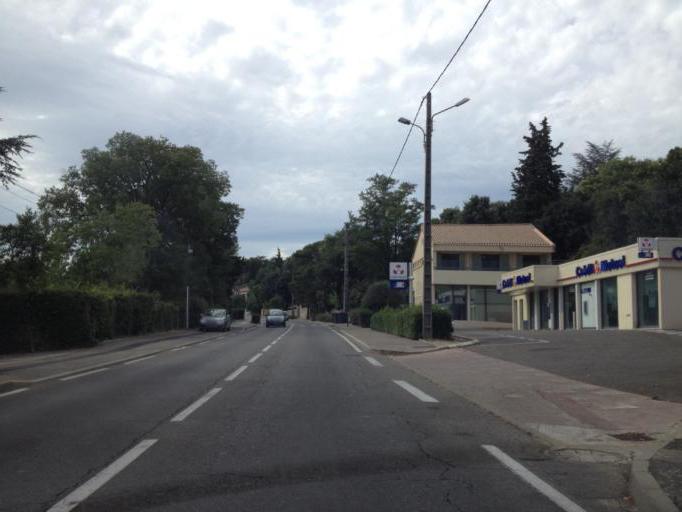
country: FR
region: Languedoc-Roussillon
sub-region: Departement du Gard
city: Villeneuve-les-Avignon
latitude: 43.9569
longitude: 4.7834
